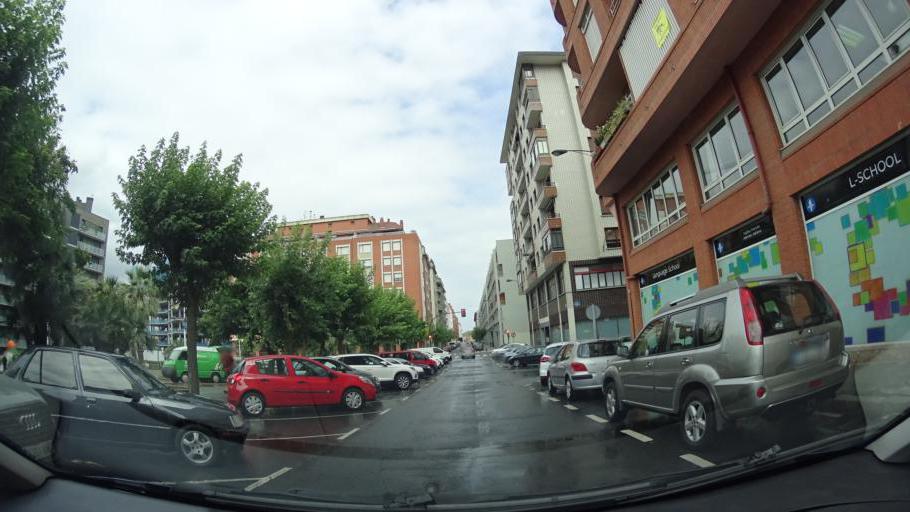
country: ES
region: Basque Country
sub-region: Bizkaia
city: Erandio
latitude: 43.2745
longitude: -2.9610
